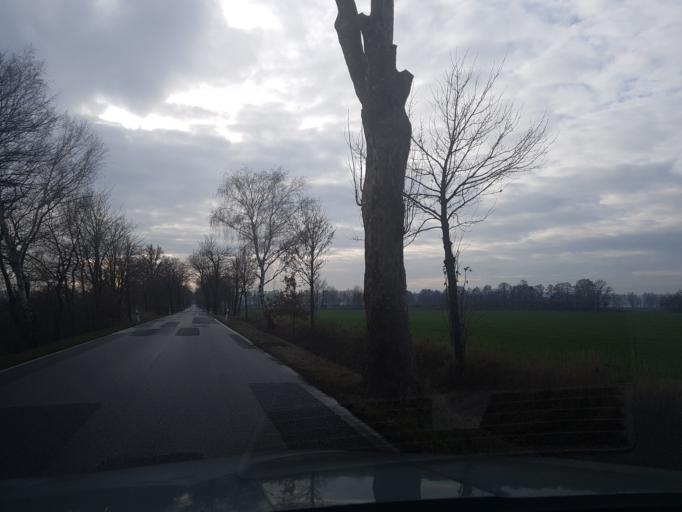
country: DE
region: Brandenburg
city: Hirschfeld
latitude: 51.4191
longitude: 13.6222
